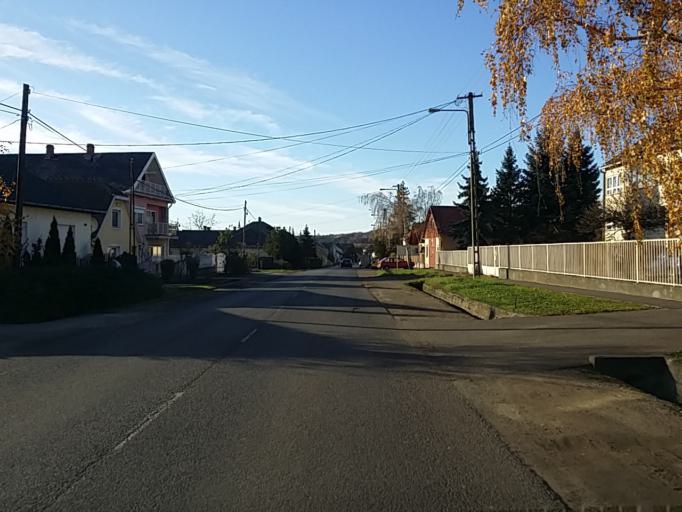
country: HU
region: Heves
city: Abasar
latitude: 47.8010
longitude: 20.0038
